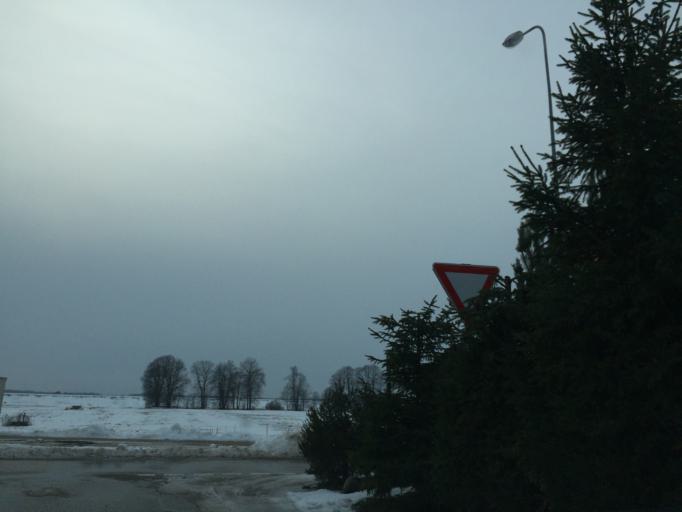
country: LV
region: Ikskile
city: Ikskile
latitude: 56.8385
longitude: 24.4755
